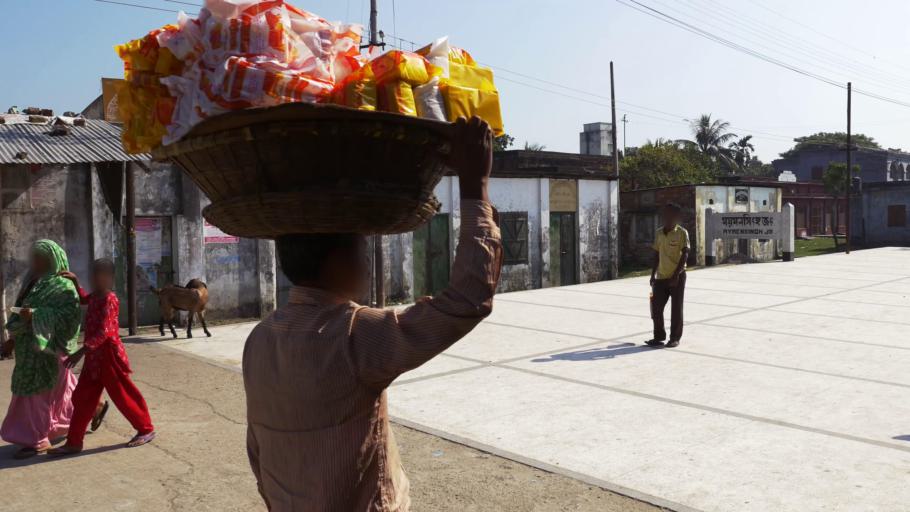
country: BD
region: Dhaka
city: Mymensingh
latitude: 24.6588
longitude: 90.4542
